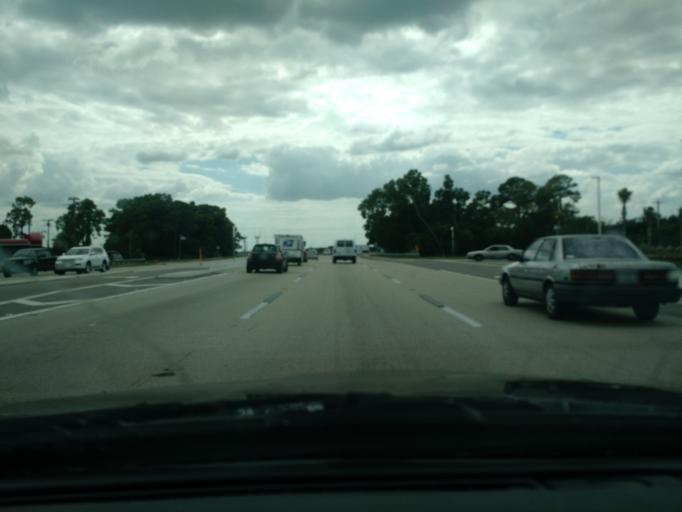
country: US
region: Florida
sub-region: Lee County
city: Pine Manor
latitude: 26.5962
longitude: -81.8634
